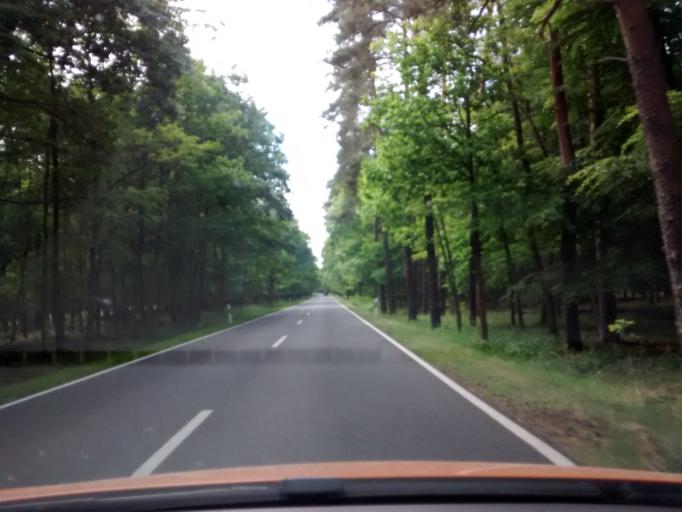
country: DE
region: Brandenburg
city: Ihlow
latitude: 51.9929
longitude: 13.2590
